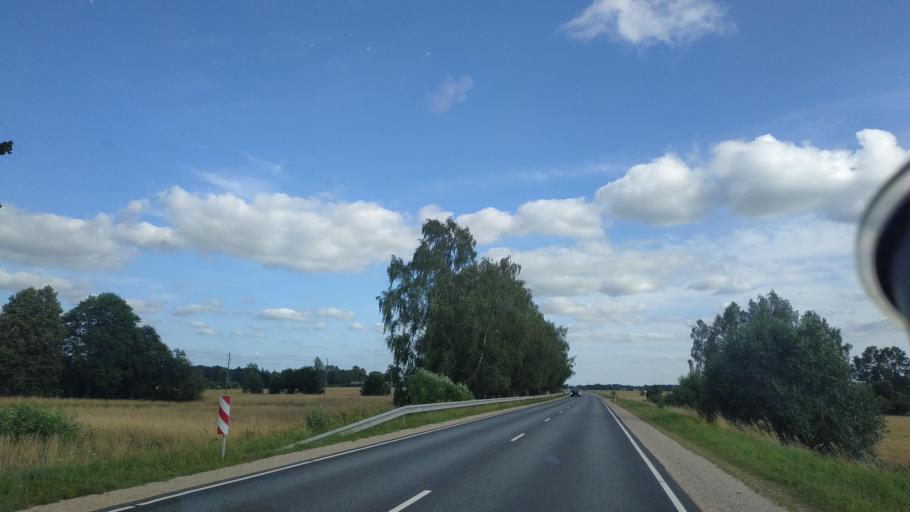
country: LV
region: Tukuma Rajons
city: Tukums
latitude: 56.9262
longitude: 23.2046
